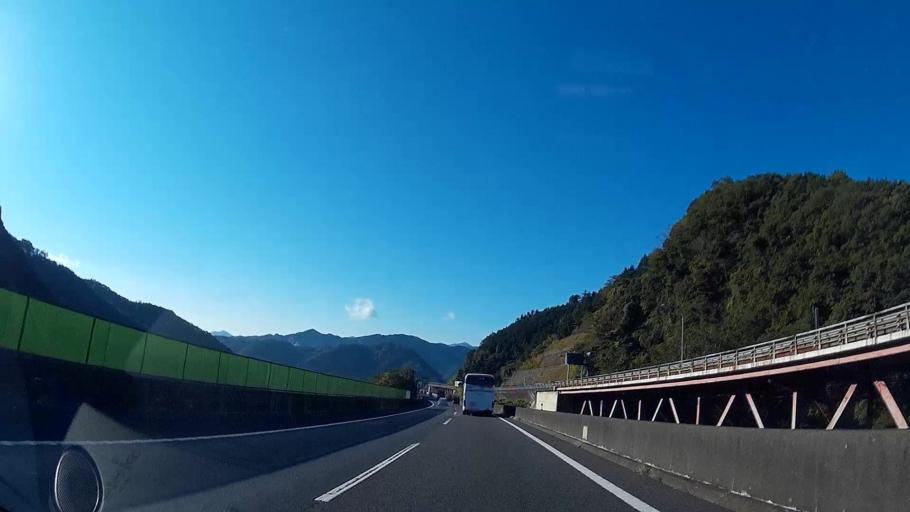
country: JP
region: Yamanashi
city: Uenohara
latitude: 35.6306
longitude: 139.2039
